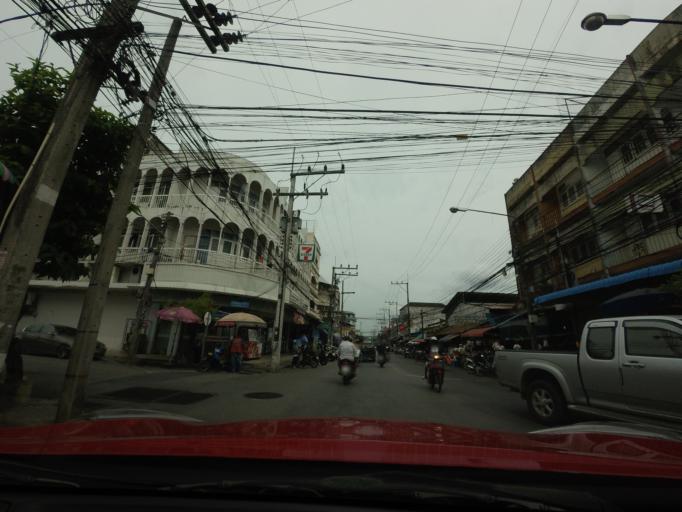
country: TH
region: Songkhla
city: Hat Yai
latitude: 6.9949
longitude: 100.4753
